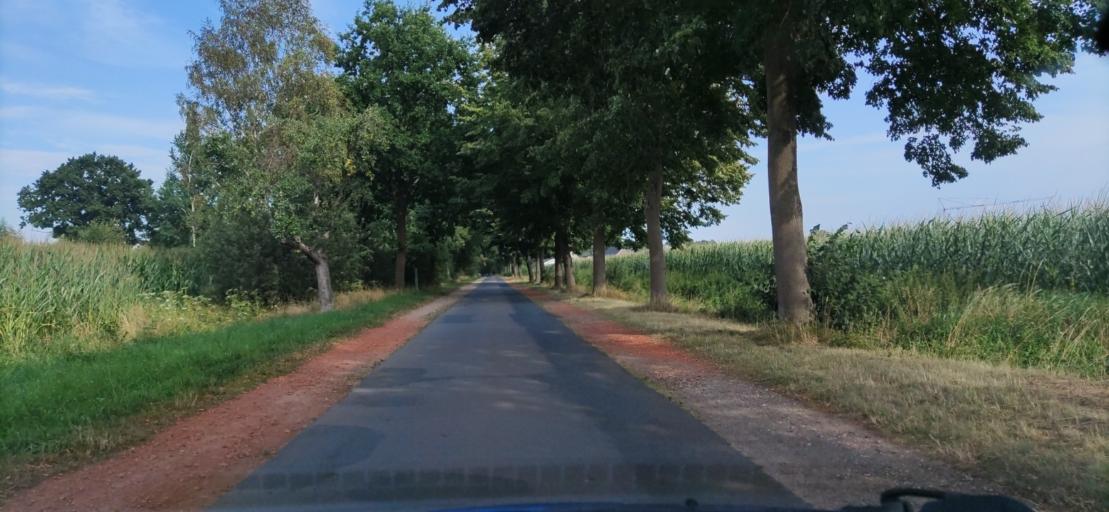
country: DE
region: Lower Saxony
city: Bleckede
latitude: 53.2891
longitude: 10.7176
